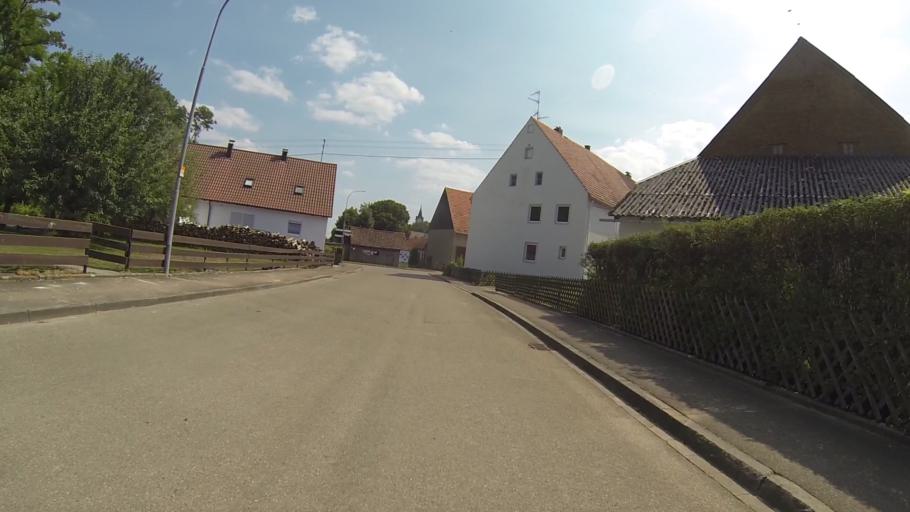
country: DE
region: Baden-Wuerttemberg
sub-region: Regierungsbezirk Stuttgart
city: Niederstotzingen
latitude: 48.5116
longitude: 10.2589
